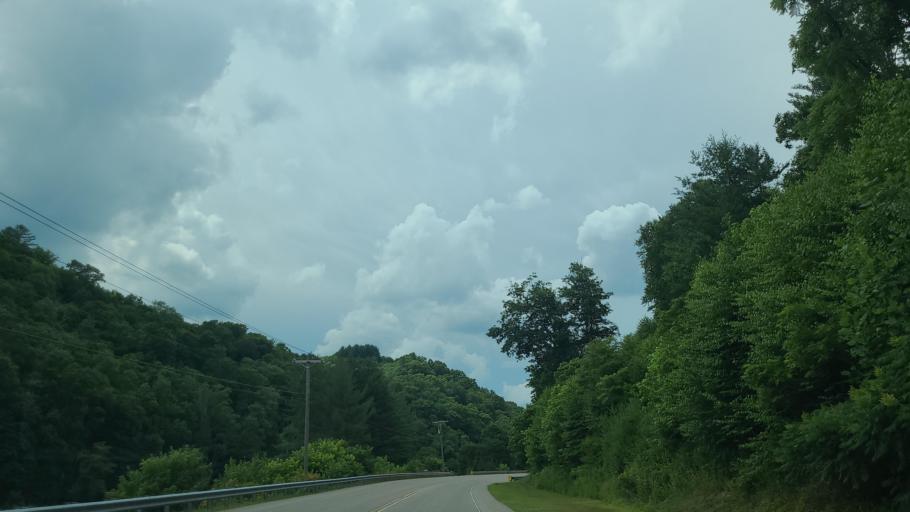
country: US
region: North Carolina
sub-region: Ashe County
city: Jefferson
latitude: 36.3792
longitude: -81.3994
